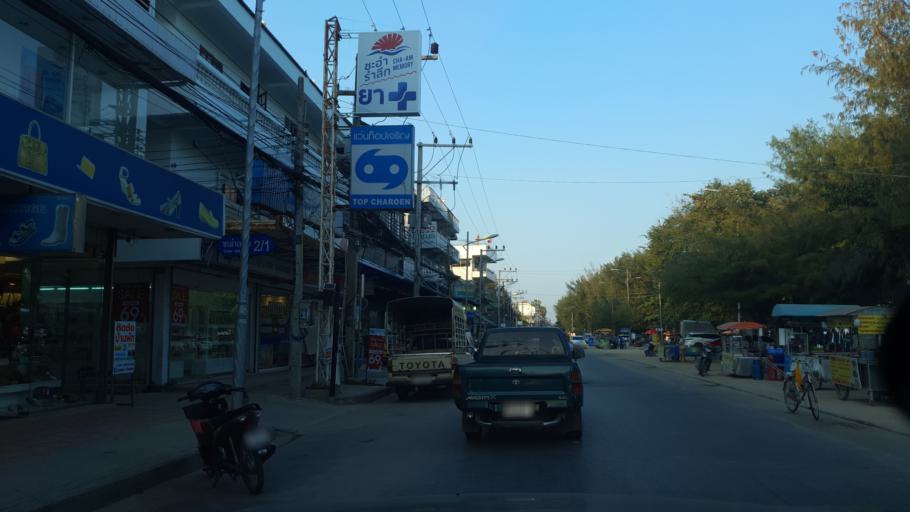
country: TH
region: Phetchaburi
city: Cha-am
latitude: 12.7968
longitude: 99.9846
